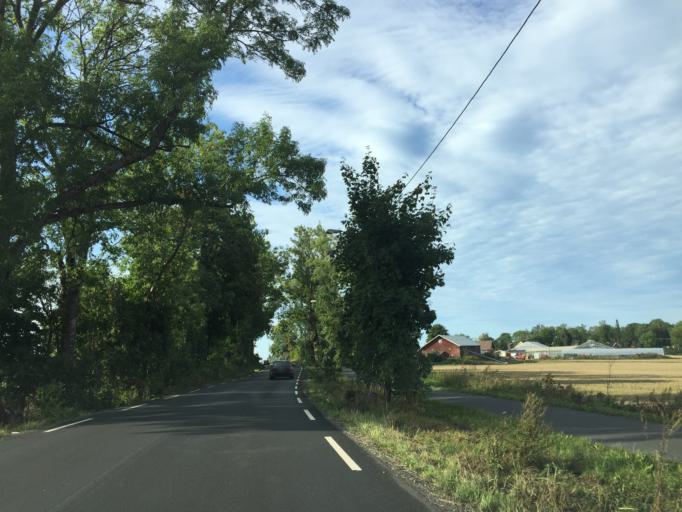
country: NO
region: Akershus
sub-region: As
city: As
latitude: 59.7088
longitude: 10.7718
